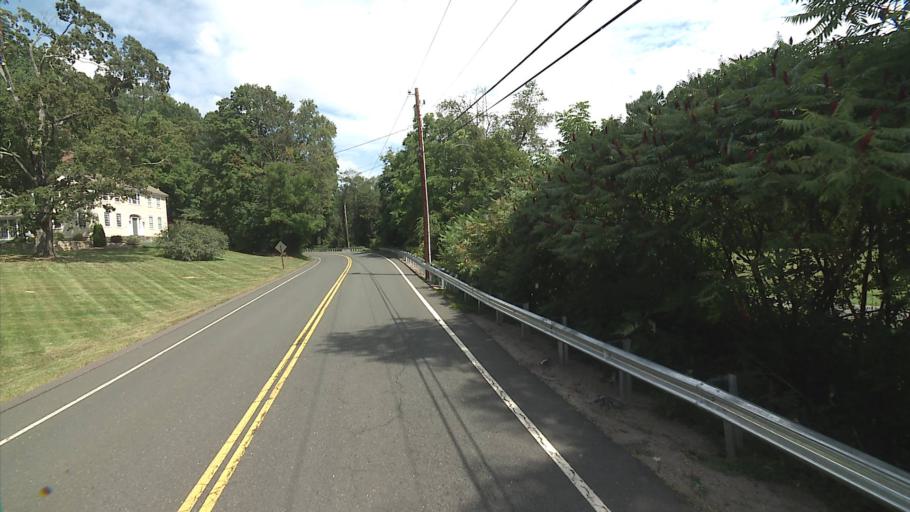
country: US
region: Massachusetts
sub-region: Hampden County
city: Granville
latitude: 42.0267
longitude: -72.8611
